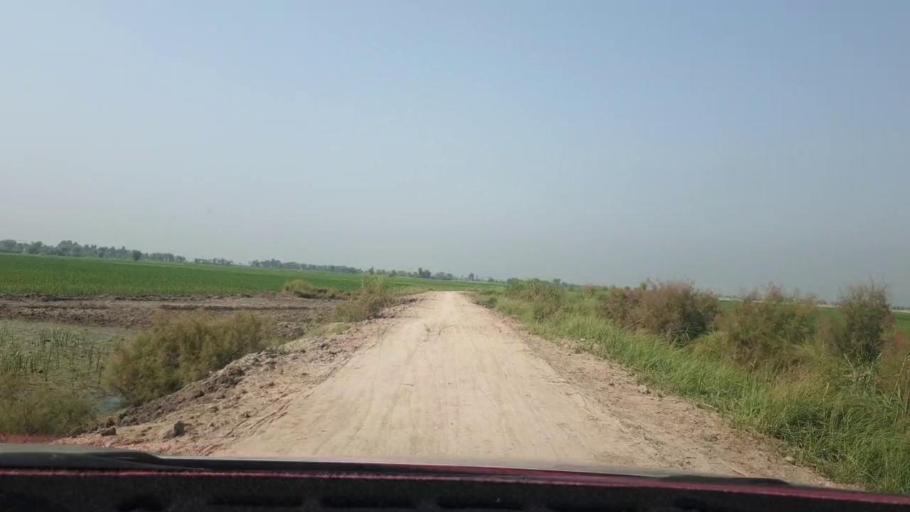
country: PK
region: Sindh
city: Nasirabad
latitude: 27.4230
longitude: 67.9402
